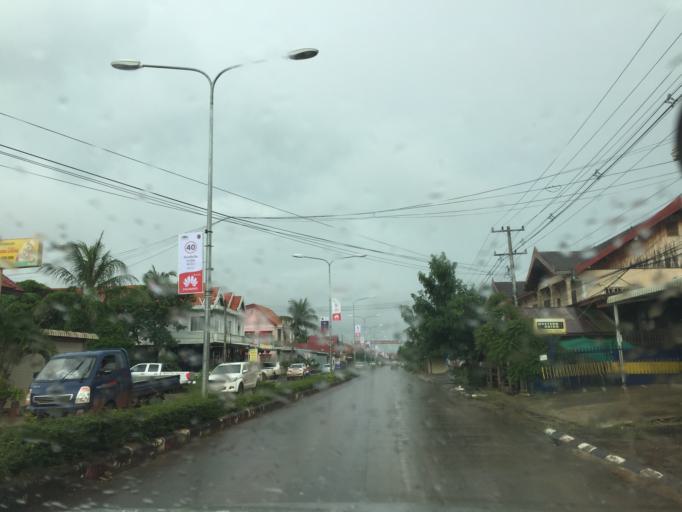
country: LA
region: Attapu
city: Attapu
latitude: 14.8202
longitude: 106.8128
